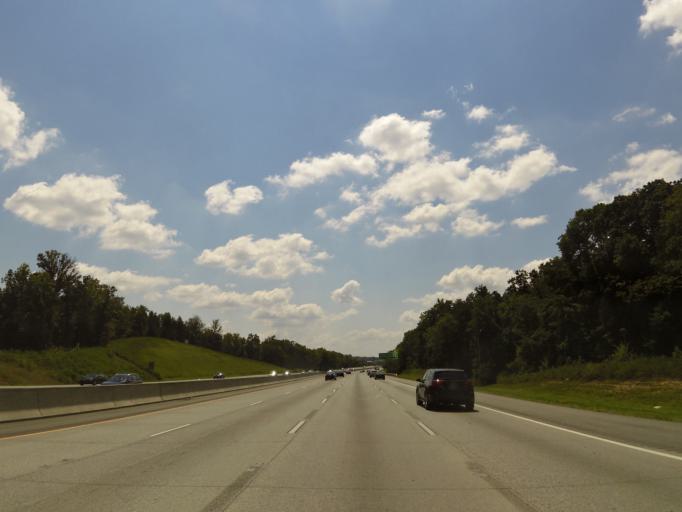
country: US
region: North Carolina
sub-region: Cabarrus County
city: Harrisburg
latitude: 35.3812
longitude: -80.7062
